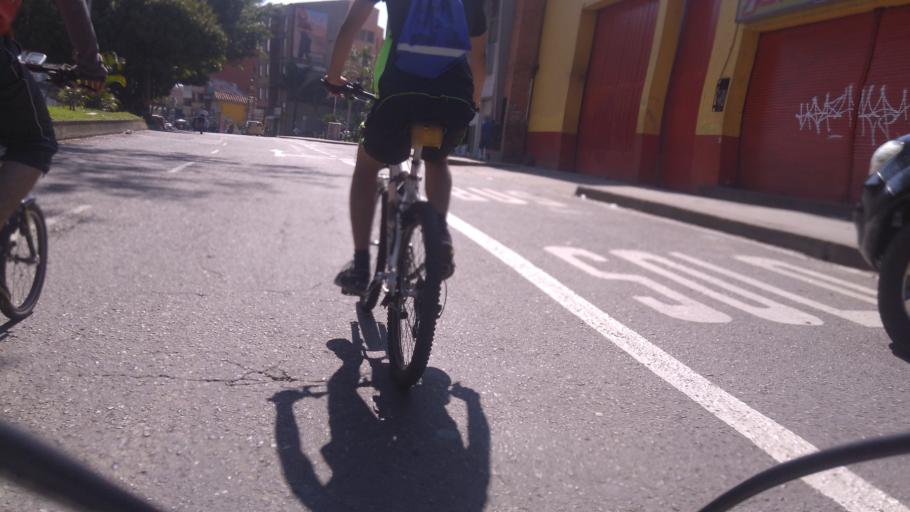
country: CO
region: Antioquia
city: Medellin
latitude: 6.2514
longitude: -75.6065
